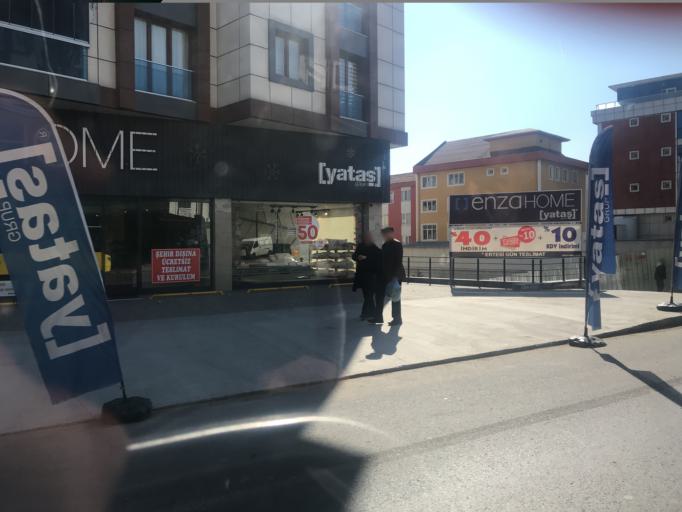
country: TR
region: Istanbul
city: Pendik
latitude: 40.8979
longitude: 29.2546
